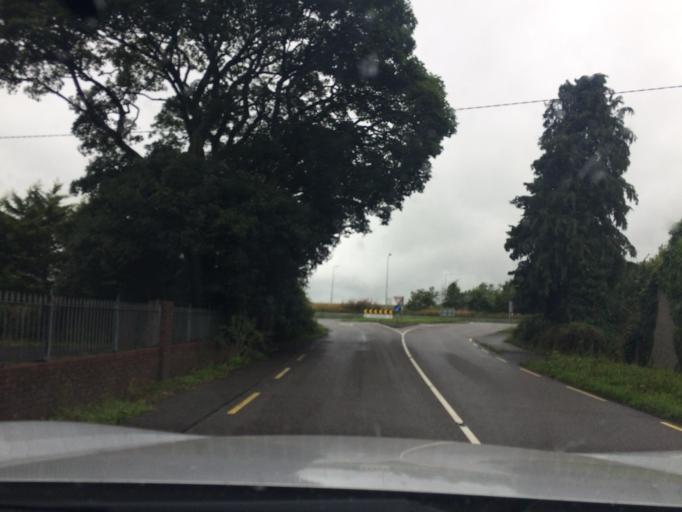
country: IE
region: Munster
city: Cashel
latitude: 52.5065
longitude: -7.8723
